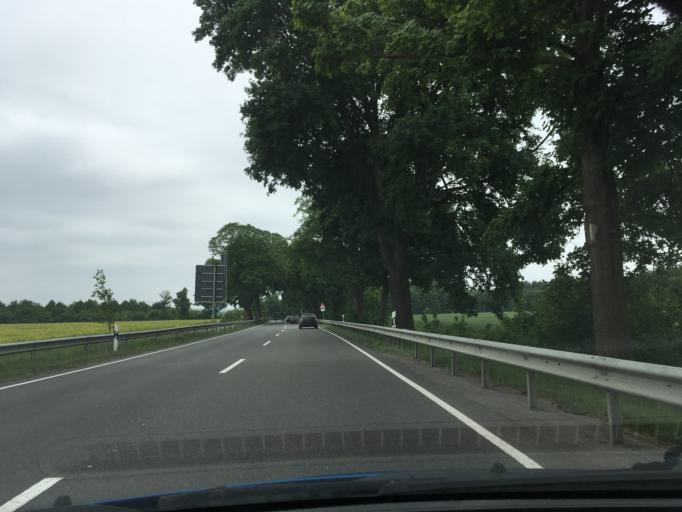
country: DE
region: Lower Saxony
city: Buchholz in der Nordheide
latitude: 53.3585
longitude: 9.8665
